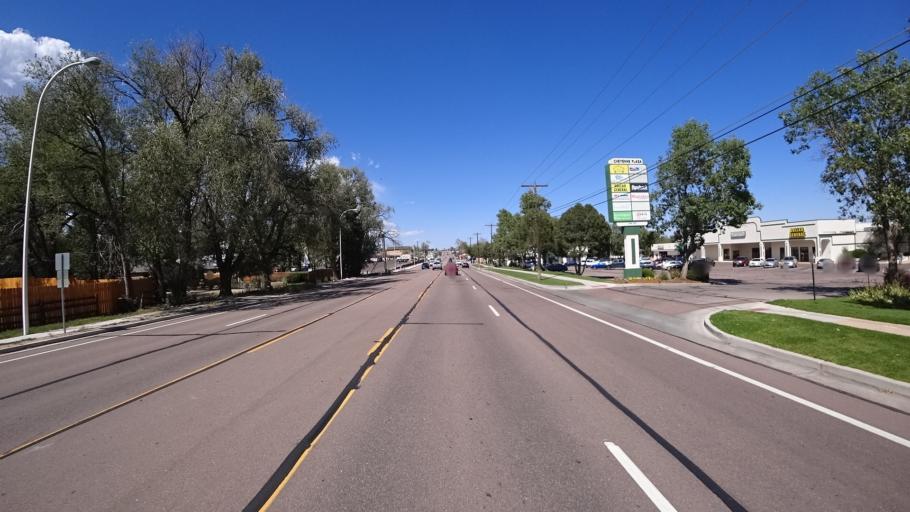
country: US
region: Colorado
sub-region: El Paso County
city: Colorado Springs
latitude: 38.8046
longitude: -104.8408
